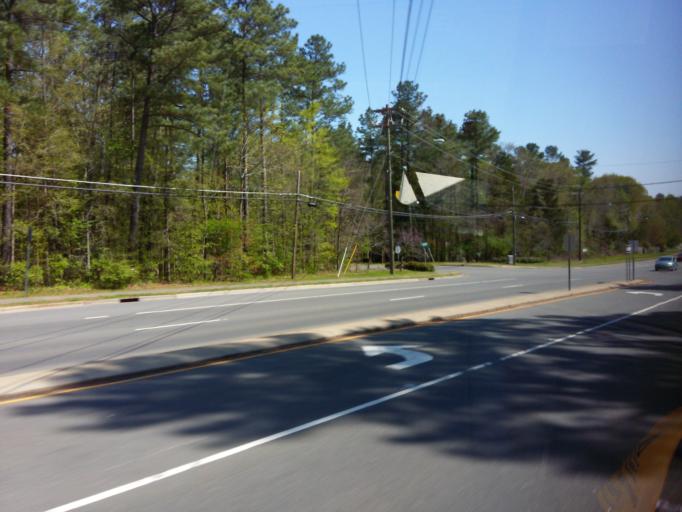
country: US
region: North Carolina
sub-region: Orange County
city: Chapel Hill
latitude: 35.9558
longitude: -79.0580
